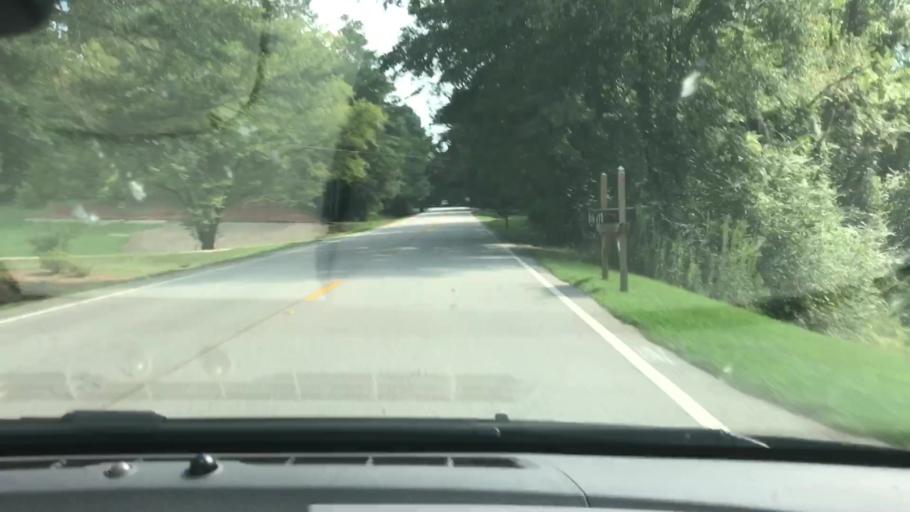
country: US
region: Georgia
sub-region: Troup County
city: La Grange
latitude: 33.1228
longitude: -85.0893
